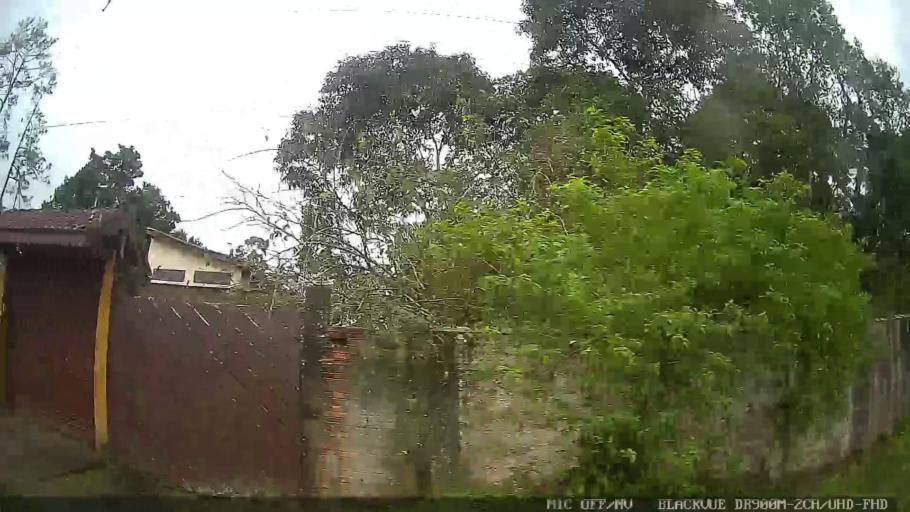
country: BR
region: Sao Paulo
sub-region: Itanhaem
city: Itanhaem
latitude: -24.1747
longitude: -46.8274
